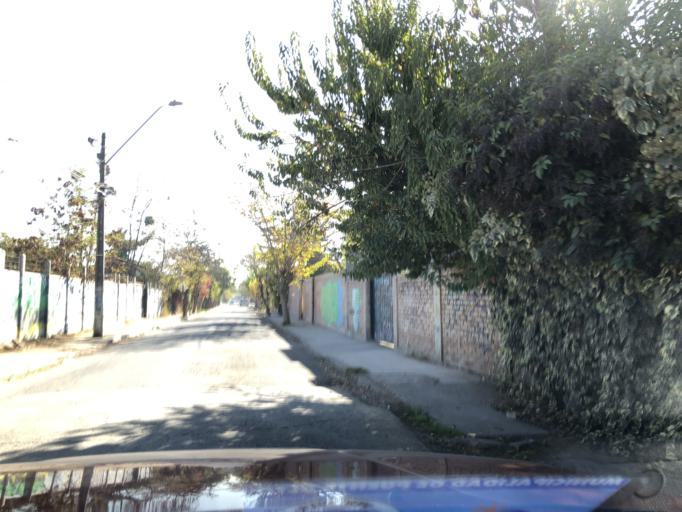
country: CL
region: Santiago Metropolitan
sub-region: Provincia de Cordillera
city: Puente Alto
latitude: -33.5857
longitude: -70.5740
